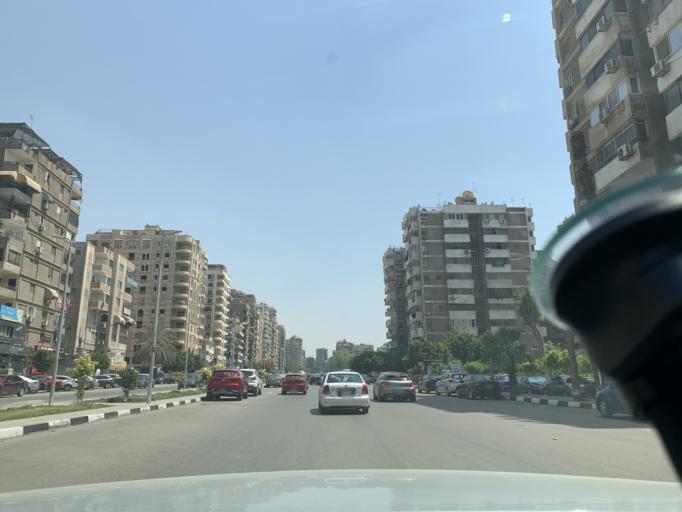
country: EG
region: Muhafazat al Qahirah
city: Cairo
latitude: 30.0667
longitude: 31.3489
